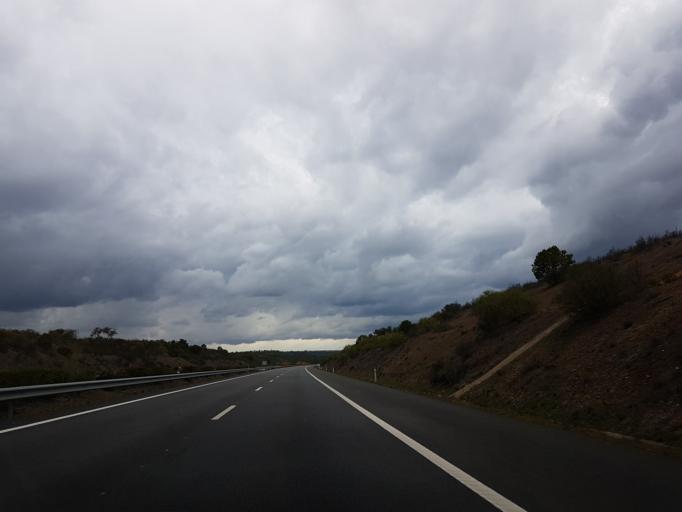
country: PT
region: Setubal
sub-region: Grandola
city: Grandola
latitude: 38.0916
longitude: -8.3878
